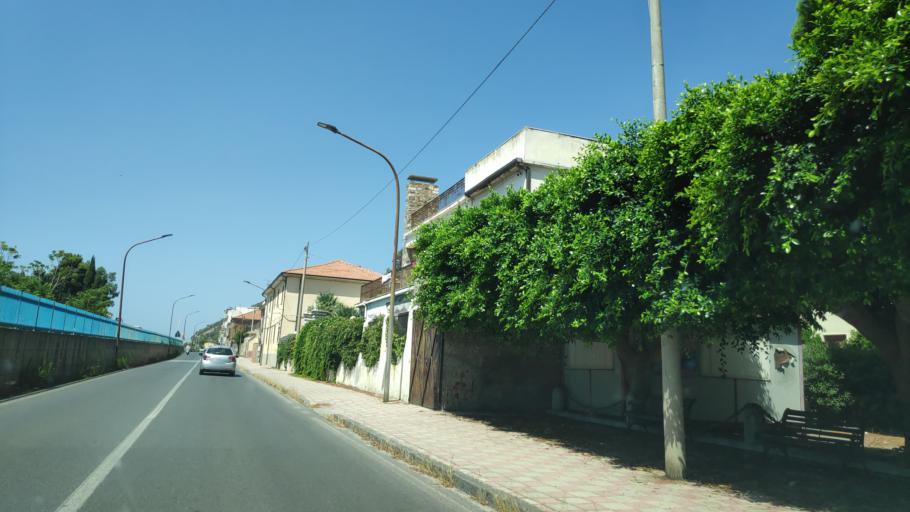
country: IT
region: Calabria
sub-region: Provincia di Reggio Calabria
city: Palizzi Marina
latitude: 37.9193
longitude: 15.9814
